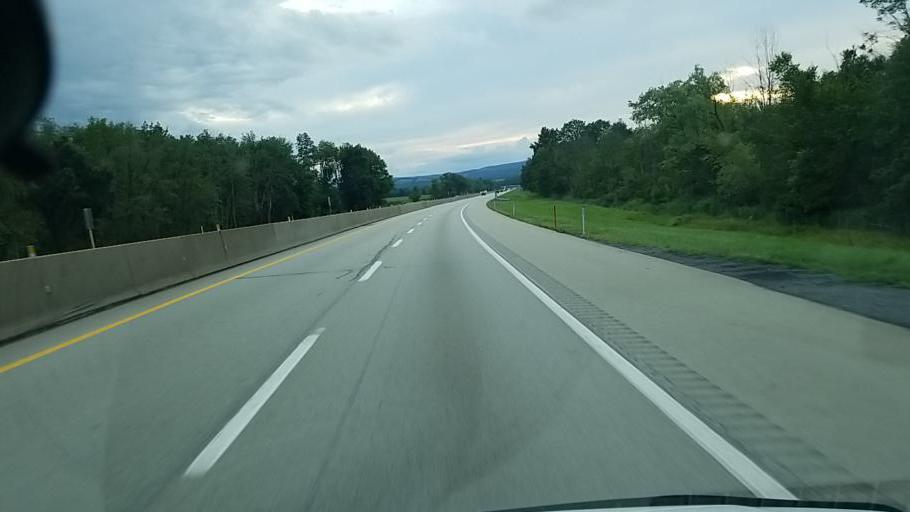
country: US
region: Pennsylvania
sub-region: Bedford County
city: Bedford
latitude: 40.0113
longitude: -78.6512
